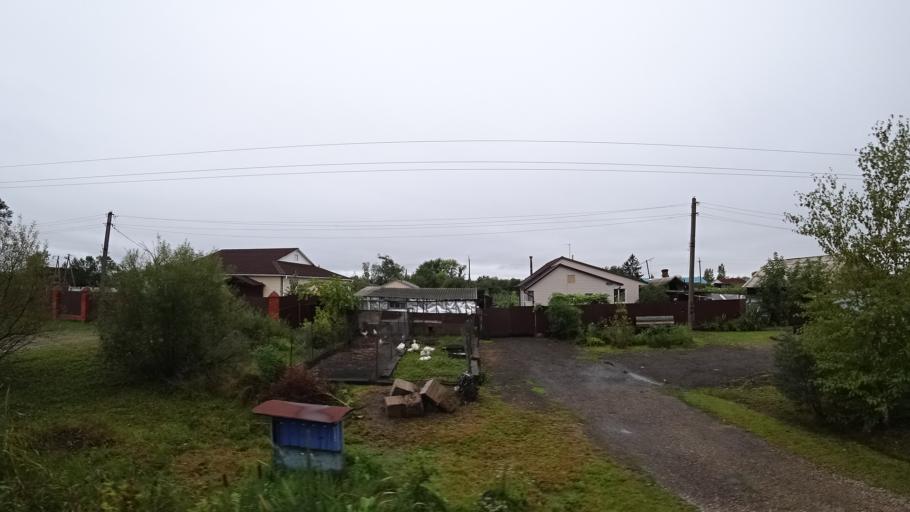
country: RU
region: Primorskiy
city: Monastyrishche
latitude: 44.2006
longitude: 132.4640
